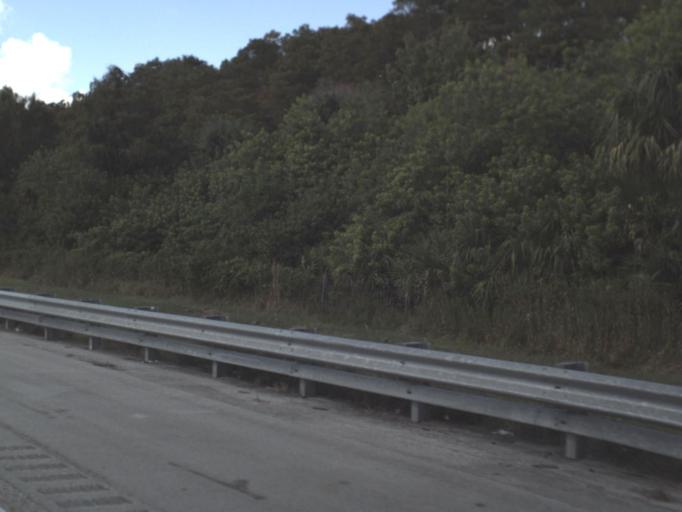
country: US
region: Florida
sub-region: Indian River County
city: West Vero Corridor
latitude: 27.5595
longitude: -80.6568
